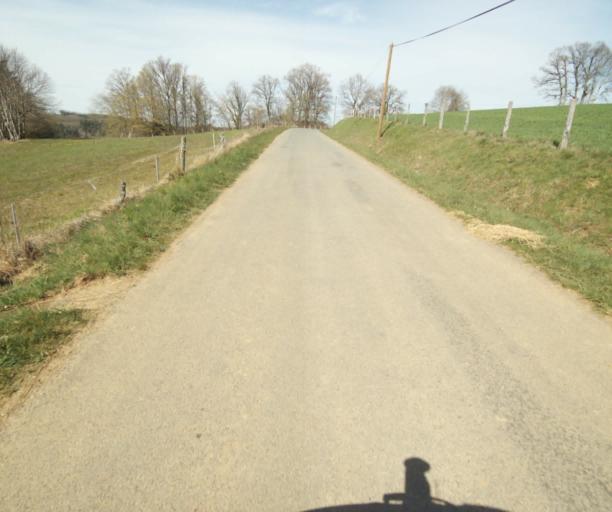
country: FR
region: Limousin
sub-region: Departement de la Correze
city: Seilhac
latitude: 45.3957
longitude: 1.7841
